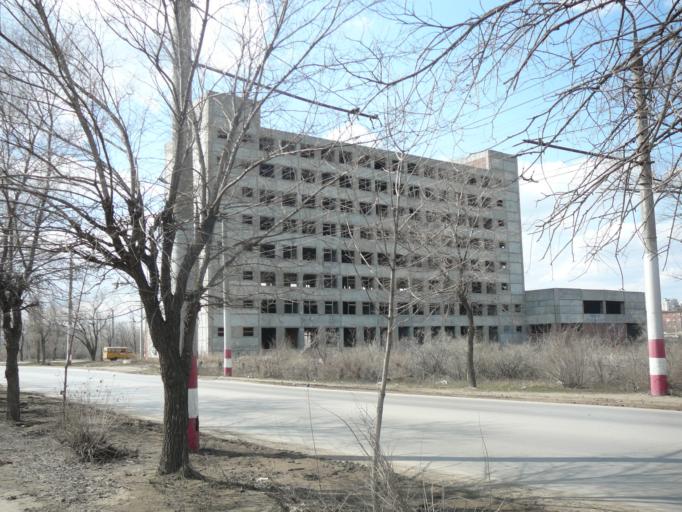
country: RU
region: Saratov
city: Engel's
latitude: 51.4666
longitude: 46.1519
